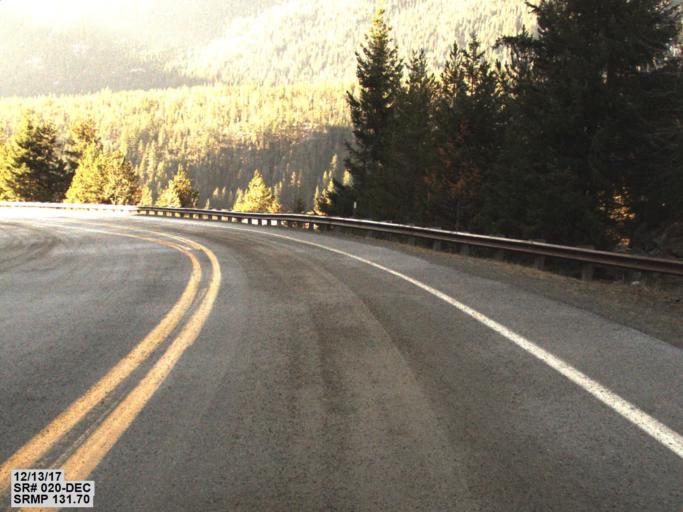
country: US
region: Washington
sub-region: Snohomish County
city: Darrington
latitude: 48.7096
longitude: -121.0962
